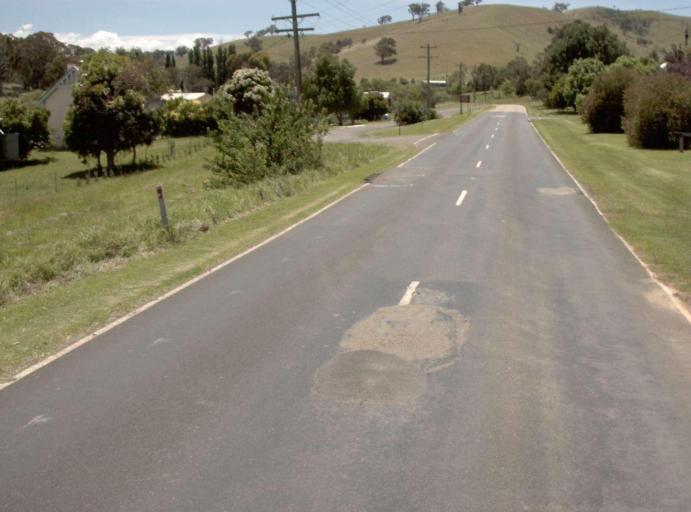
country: AU
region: Victoria
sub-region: East Gippsland
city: Bairnsdale
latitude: -37.3765
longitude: 147.8339
